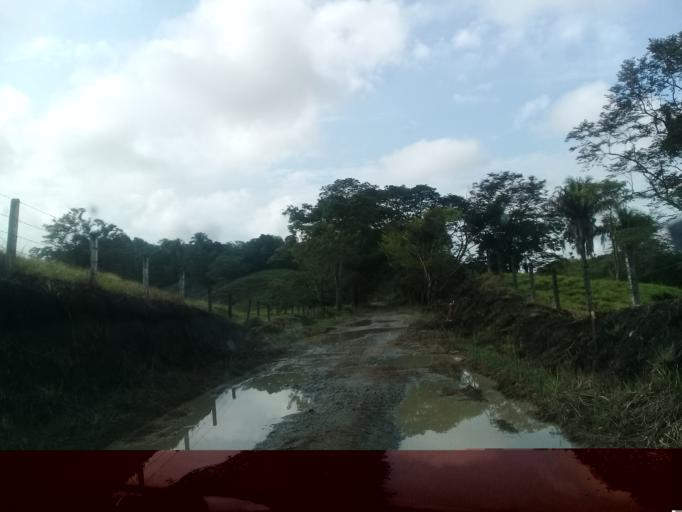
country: CO
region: Antioquia
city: Puerto Triunfo
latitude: 5.7290
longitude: -74.5221
